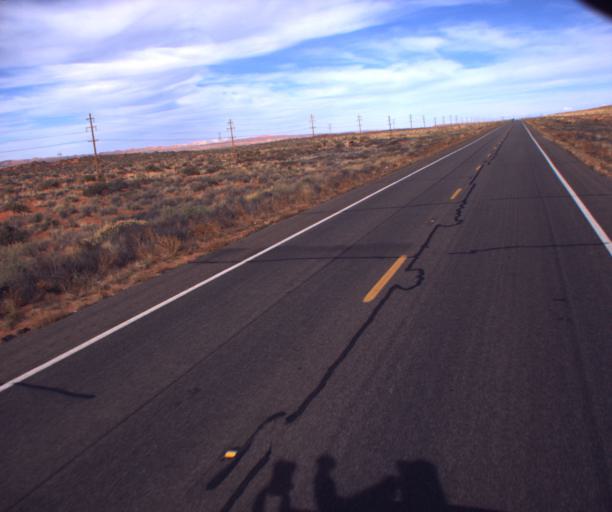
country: US
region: Arizona
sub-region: Navajo County
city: Kayenta
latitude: 36.7890
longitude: -109.9522
